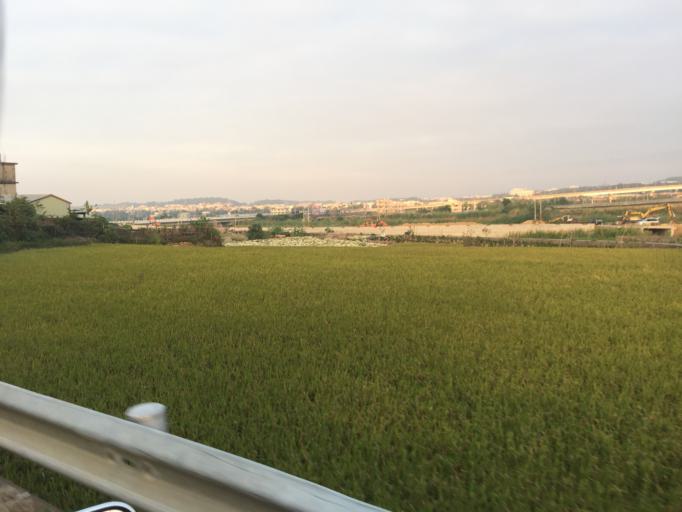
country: TW
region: Taiwan
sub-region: Miaoli
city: Miaoli
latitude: 24.4754
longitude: 120.7773
